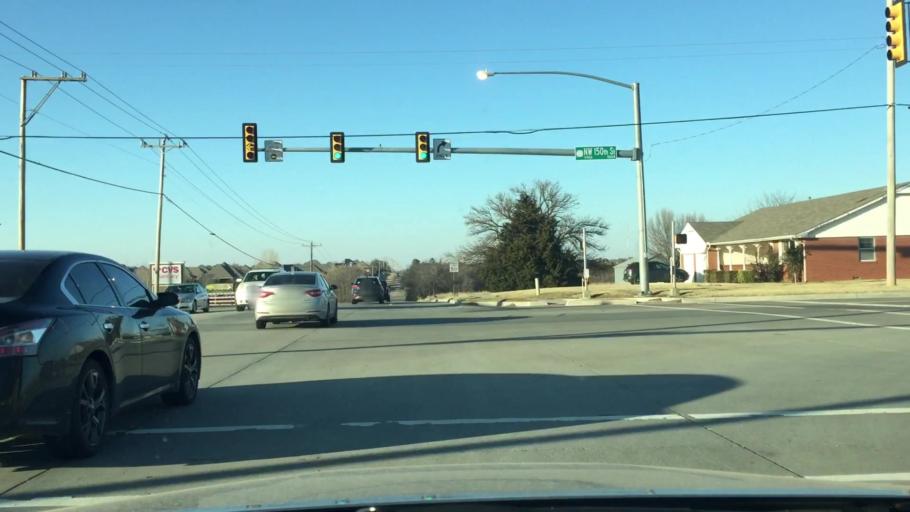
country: US
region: Oklahoma
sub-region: Oklahoma County
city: The Village
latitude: 35.6235
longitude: -97.6207
